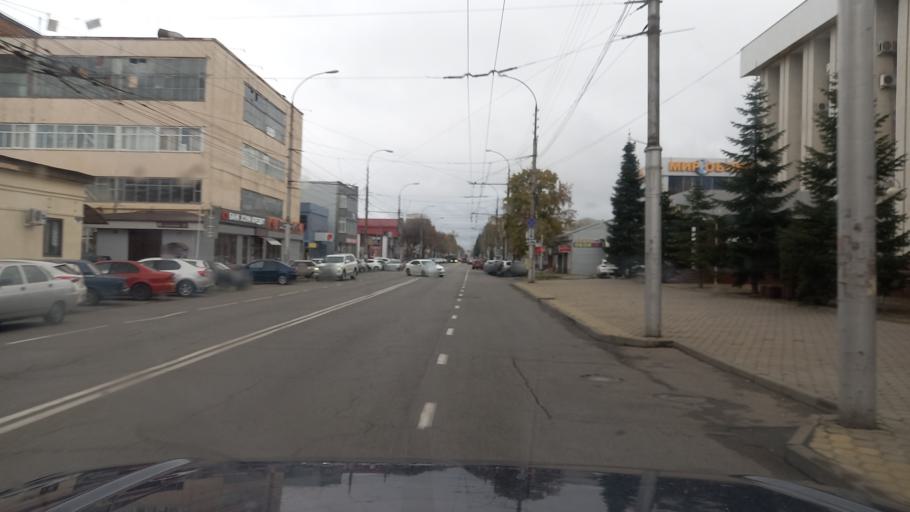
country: RU
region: Adygeya
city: Maykop
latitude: 44.6093
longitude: 40.1075
